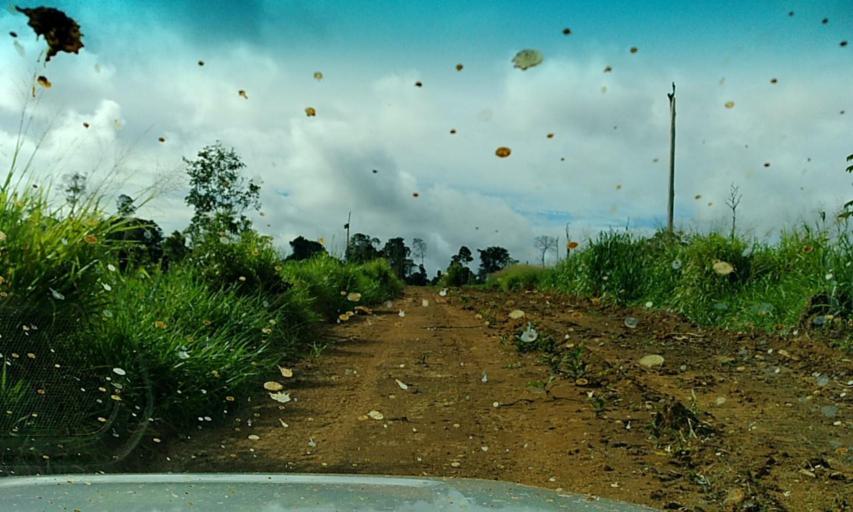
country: BR
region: Para
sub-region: Senador Jose Porfirio
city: Senador Jose Porfirio
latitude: -3.0008
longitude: -51.7402
